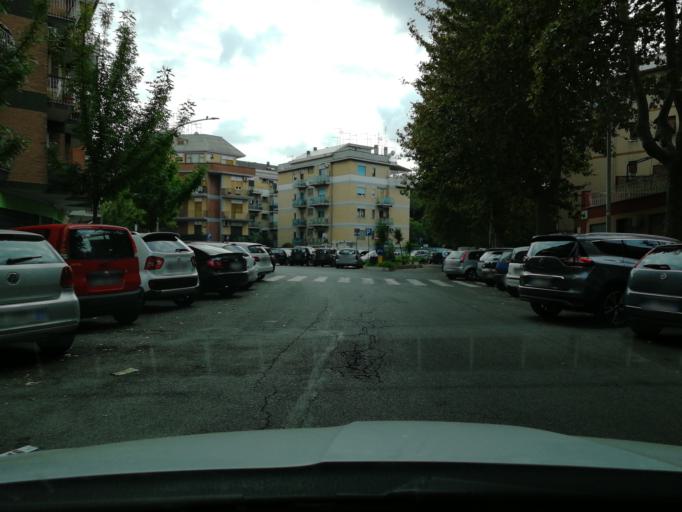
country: IT
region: Latium
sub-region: Citta metropolitana di Roma Capitale
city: Rome
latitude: 41.8627
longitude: 12.5467
